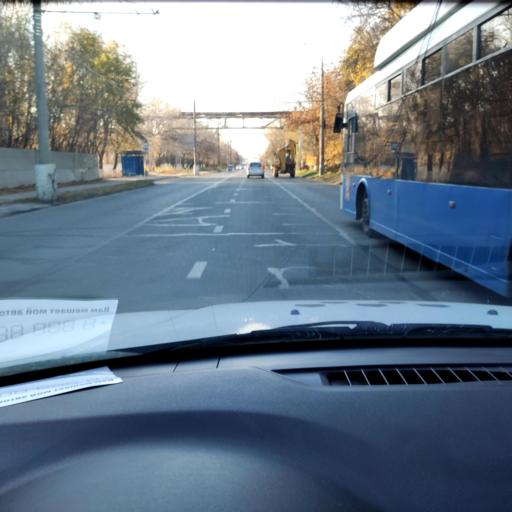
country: RU
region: Samara
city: Tol'yatti
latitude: 53.5223
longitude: 49.4333
